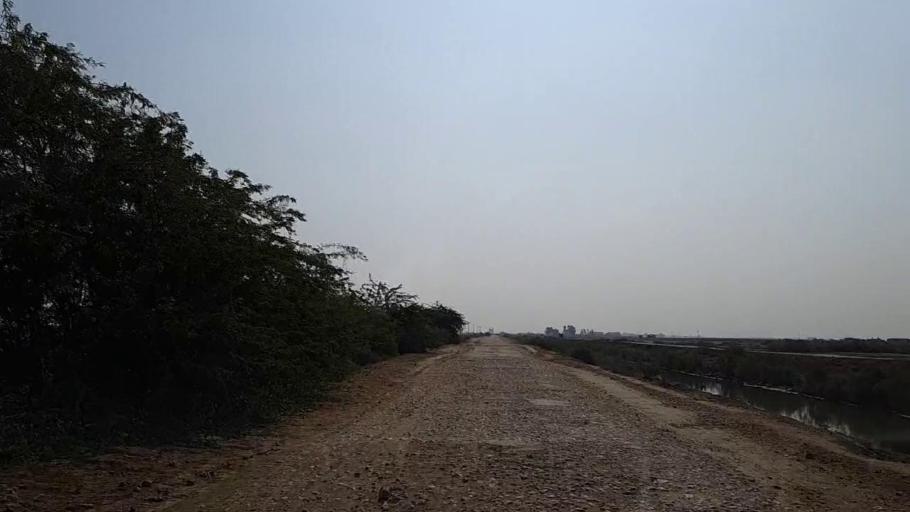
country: PK
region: Sindh
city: Thatta
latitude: 24.7182
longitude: 67.7684
